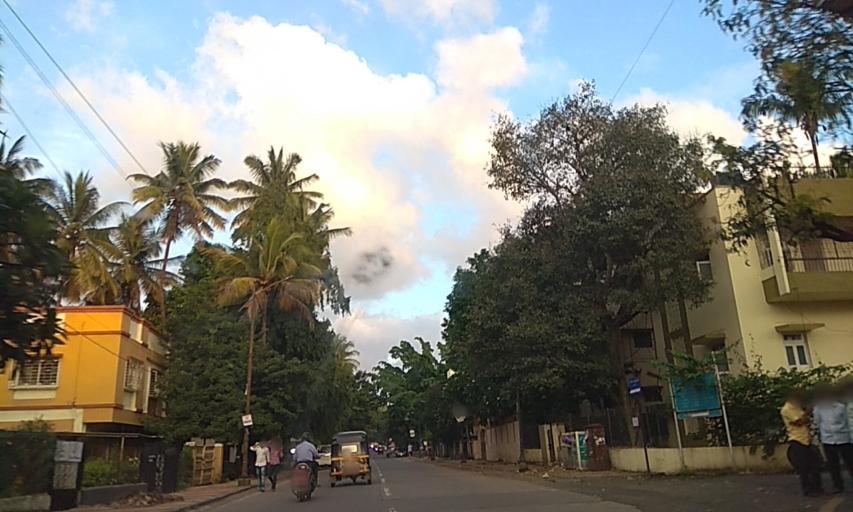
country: IN
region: Maharashtra
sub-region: Pune Division
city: Pune
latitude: 18.4927
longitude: 73.8513
